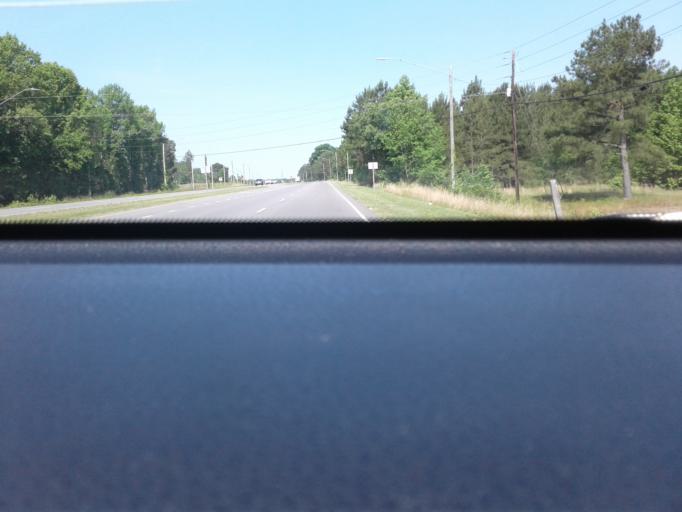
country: US
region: North Carolina
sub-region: Harnett County
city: Lillington
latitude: 35.4098
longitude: -78.7783
